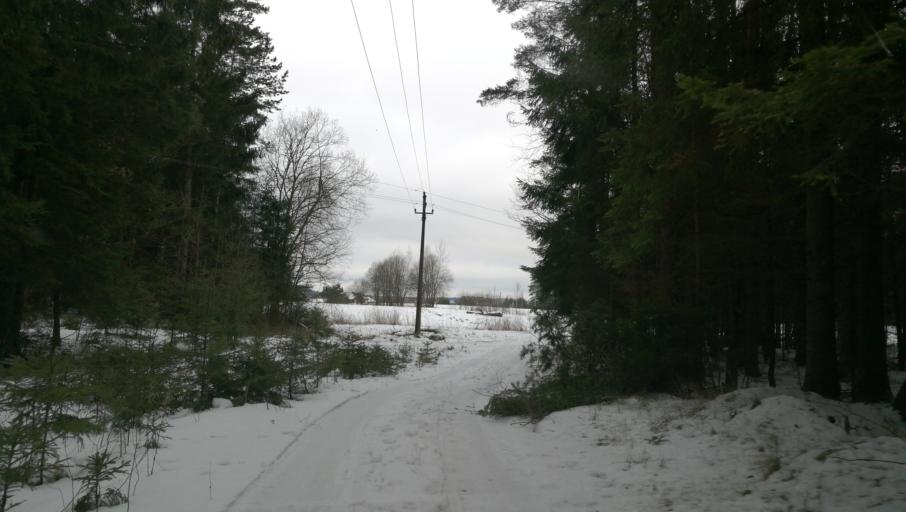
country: LT
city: Trakai
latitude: 54.6160
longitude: 24.9133
